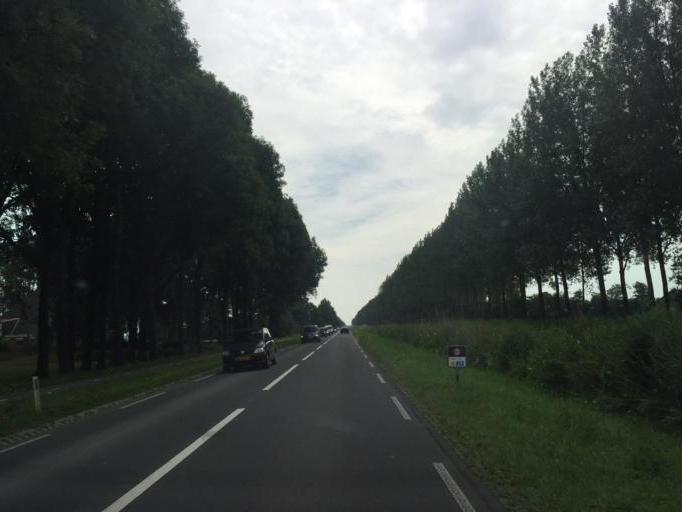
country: NL
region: North Holland
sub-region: Gemeente Heerhugowaard
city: Heerhugowaard
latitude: 52.6096
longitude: 4.8308
